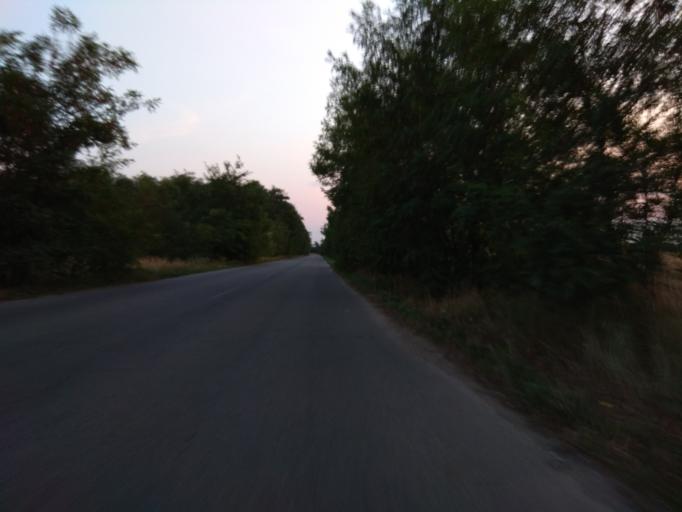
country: HU
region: Borsod-Abauj-Zemplen
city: Emod
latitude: 47.9112
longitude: 20.8587
